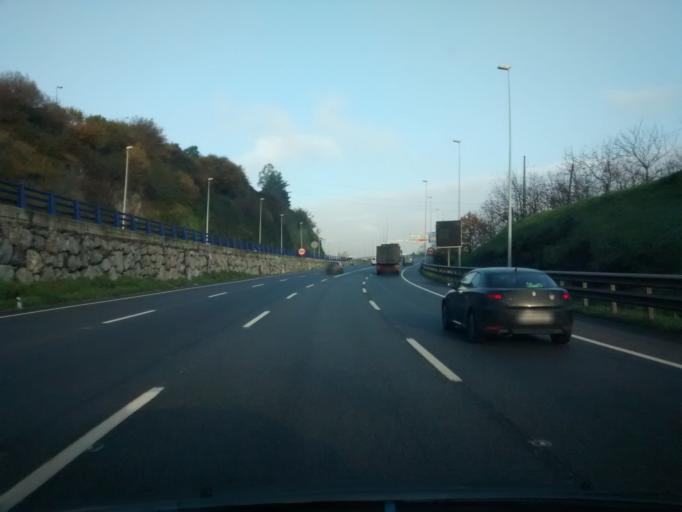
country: ES
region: Basque Country
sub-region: Bizkaia
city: Santutxu
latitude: 43.2398
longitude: -2.9263
